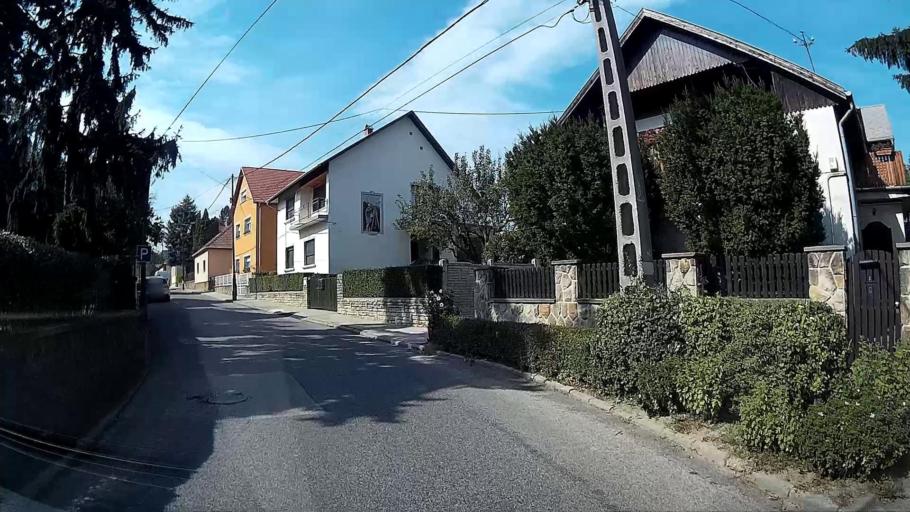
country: HU
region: Pest
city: Solymar
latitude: 47.5904
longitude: 18.9316
